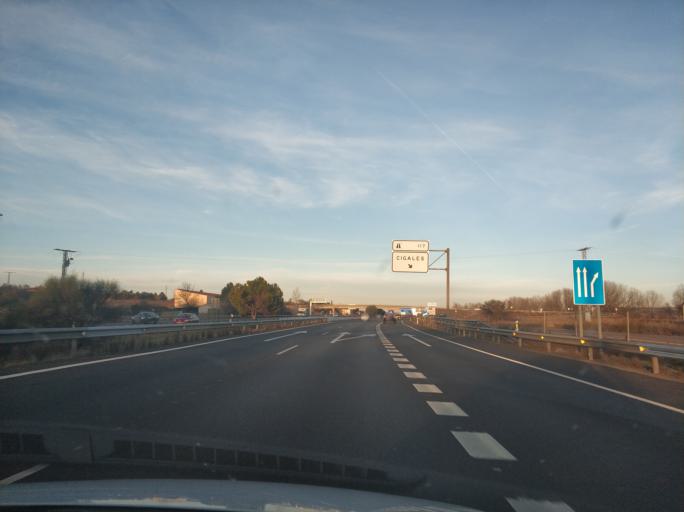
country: ES
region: Castille and Leon
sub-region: Provincia de Valladolid
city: Santovenia de Pisuerga
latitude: 41.7069
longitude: -4.7079
